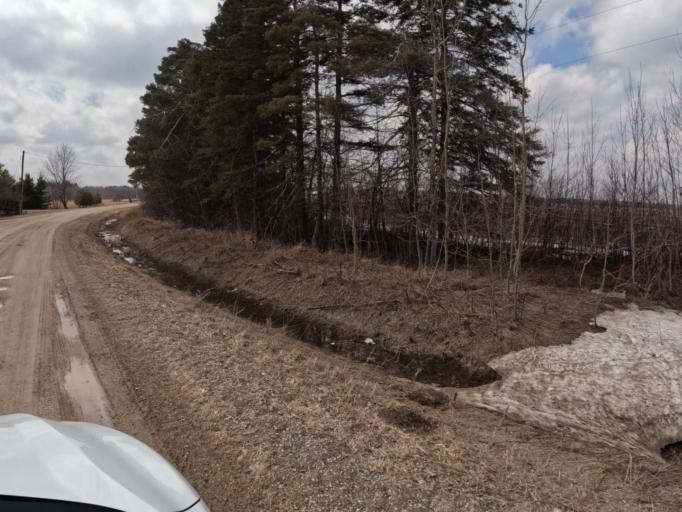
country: CA
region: Ontario
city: Shelburne
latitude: 44.0227
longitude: -80.2873
